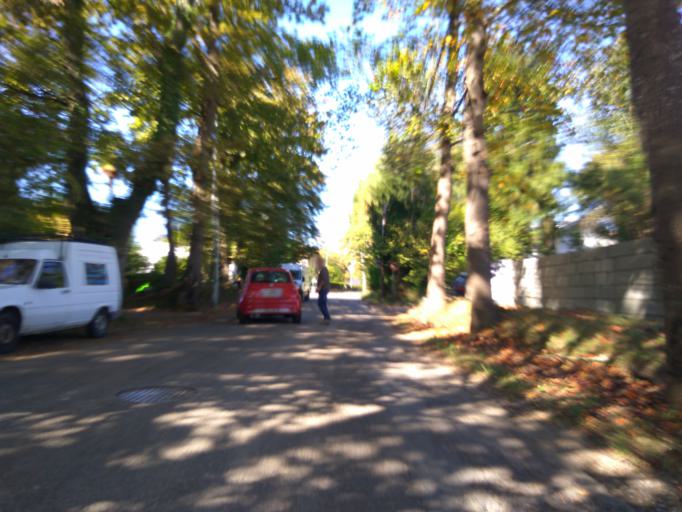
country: FR
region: Aquitaine
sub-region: Departement des Pyrenees-Atlantiques
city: Idron
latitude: 43.2986
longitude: -0.3130
